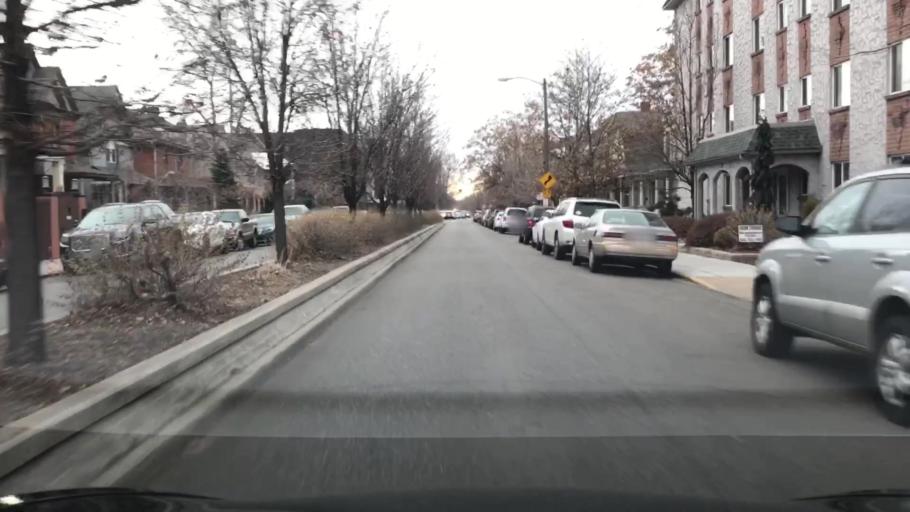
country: US
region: Colorado
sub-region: Denver County
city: Denver
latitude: 39.7163
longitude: -104.9827
